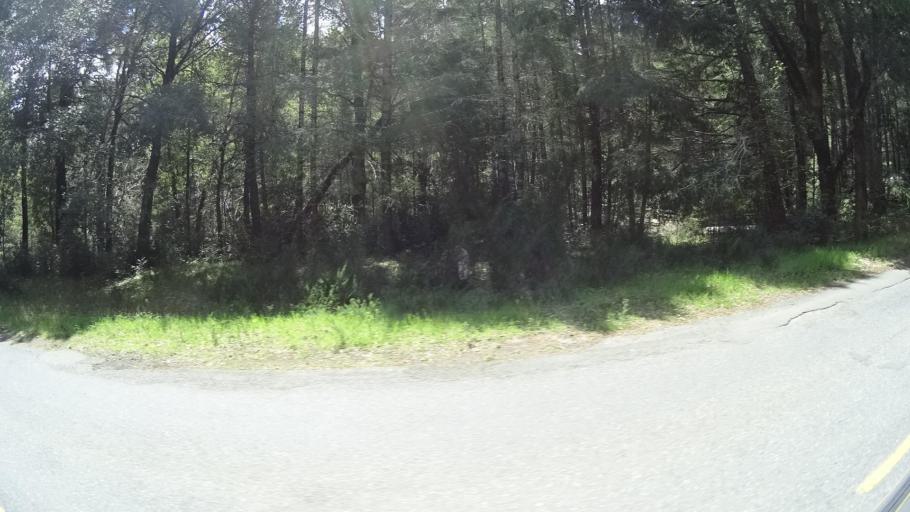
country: US
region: California
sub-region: Humboldt County
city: Redway
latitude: 40.0545
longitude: -123.9588
